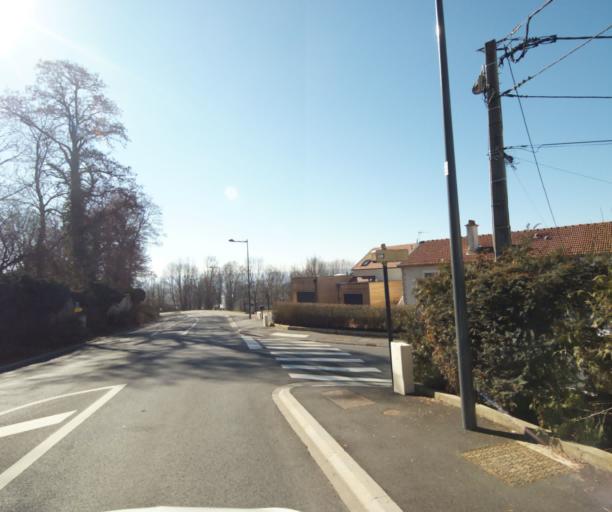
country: FR
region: Lorraine
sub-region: Departement de Meurthe-et-Moselle
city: Essey-les-Nancy
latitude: 48.7096
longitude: 6.2202
